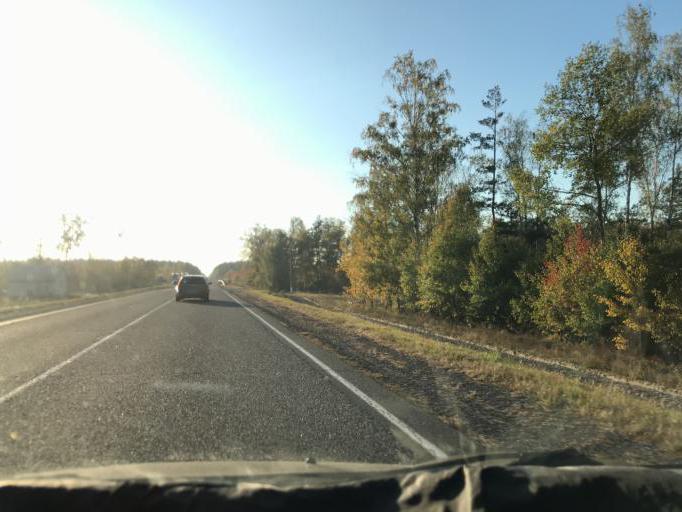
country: BY
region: Gomel
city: Zhytkavichy
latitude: 52.2700
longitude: 27.9807
